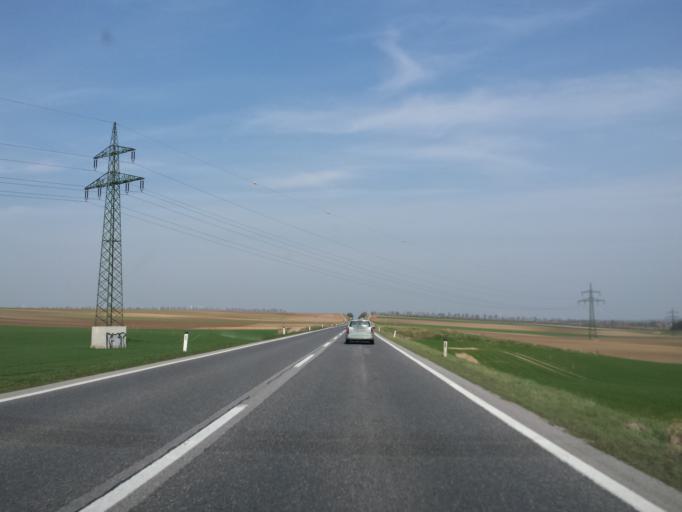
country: AT
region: Lower Austria
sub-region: Politischer Bezirk Mistelbach
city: Wilfersdorf
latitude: 48.5472
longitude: 16.6302
